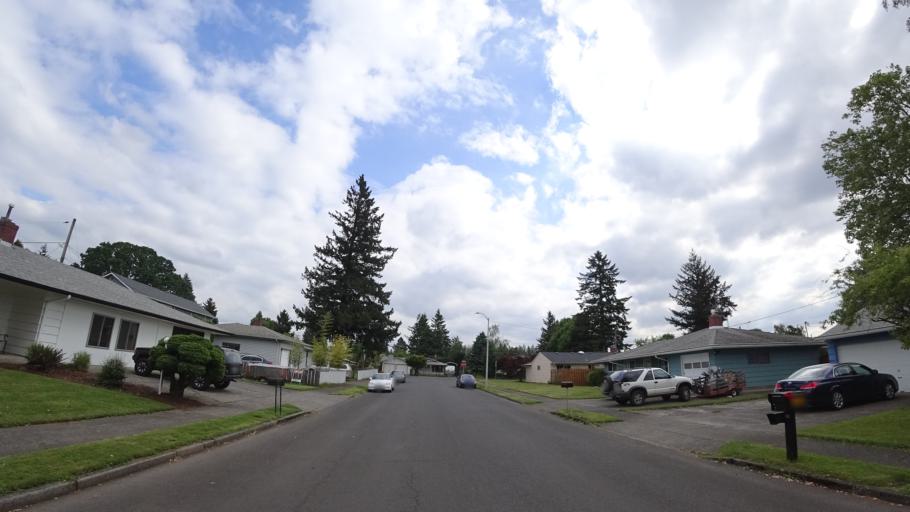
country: US
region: Oregon
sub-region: Multnomah County
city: Gresham
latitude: 45.5143
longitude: -122.4894
